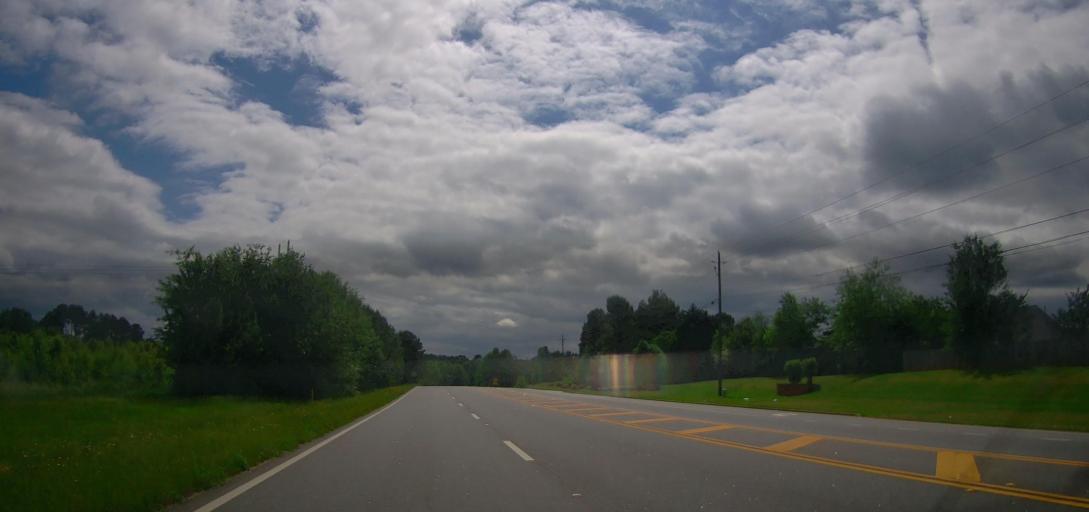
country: US
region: Georgia
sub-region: Rockdale County
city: Conyers
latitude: 33.6227
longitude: -84.0524
